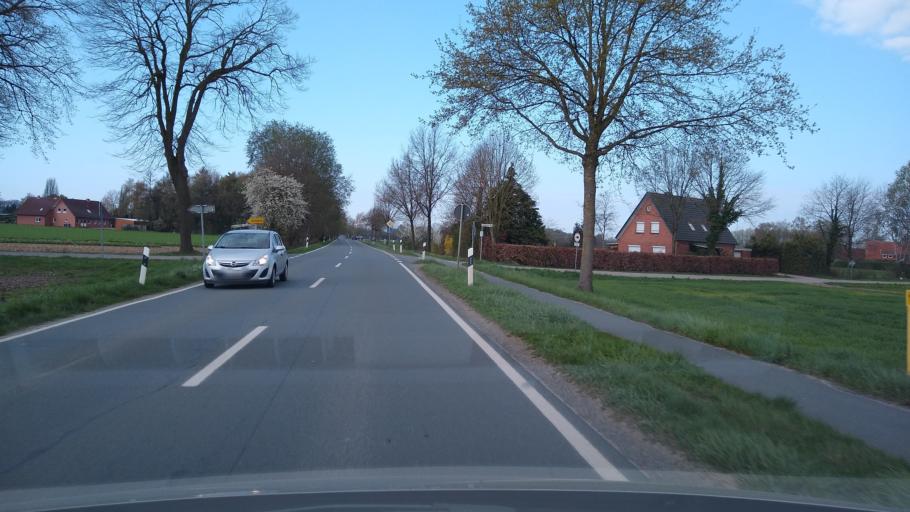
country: DE
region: Lower Saxony
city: Emstek
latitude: 52.8312
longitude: 8.1351
